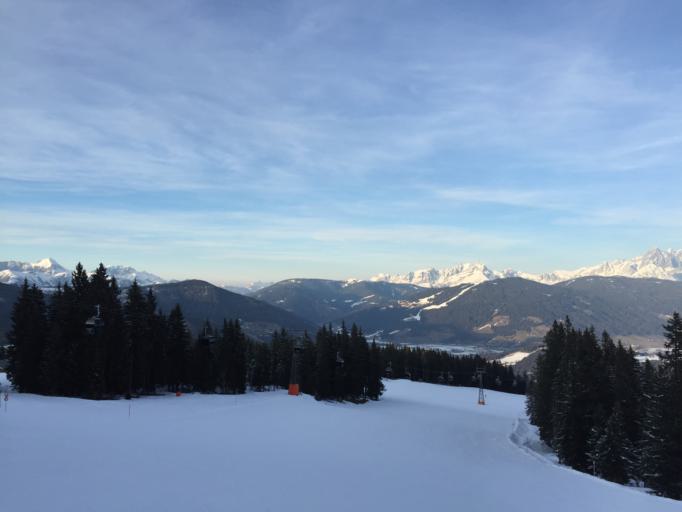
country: AT
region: Salzburg
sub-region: Politischer Bezirk Sankt Johann im Pongau
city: Flachau
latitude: 47.3366
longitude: 13.3619
